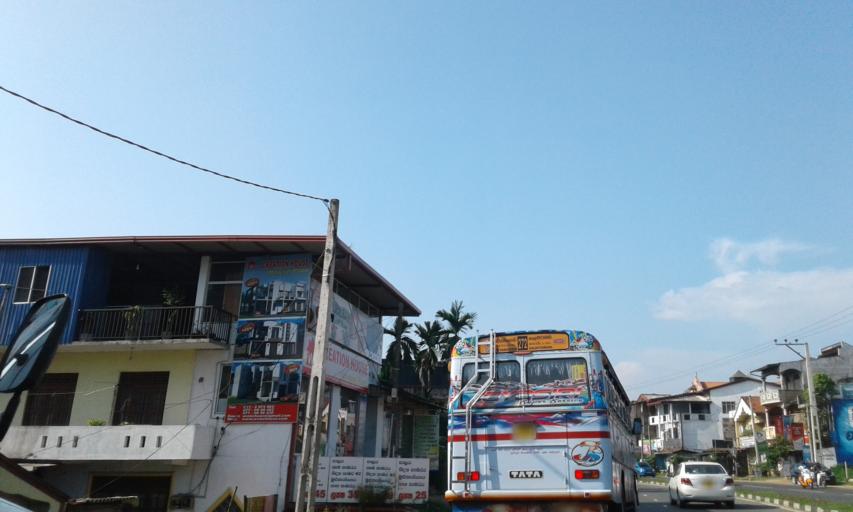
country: LK
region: Western
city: Welisara
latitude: 7.0139
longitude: 79.9676
